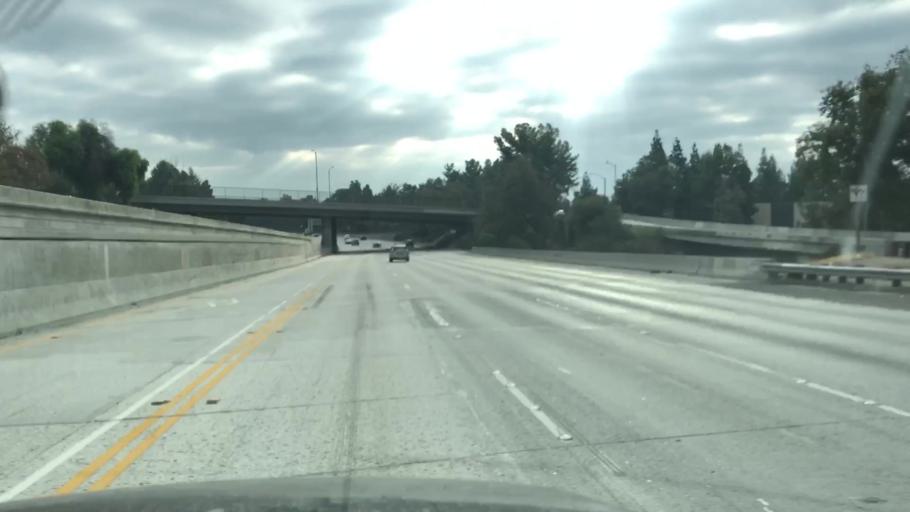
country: US
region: California
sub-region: Los Angeles County
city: Chatsworth
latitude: 34.2725
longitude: -118.5578
